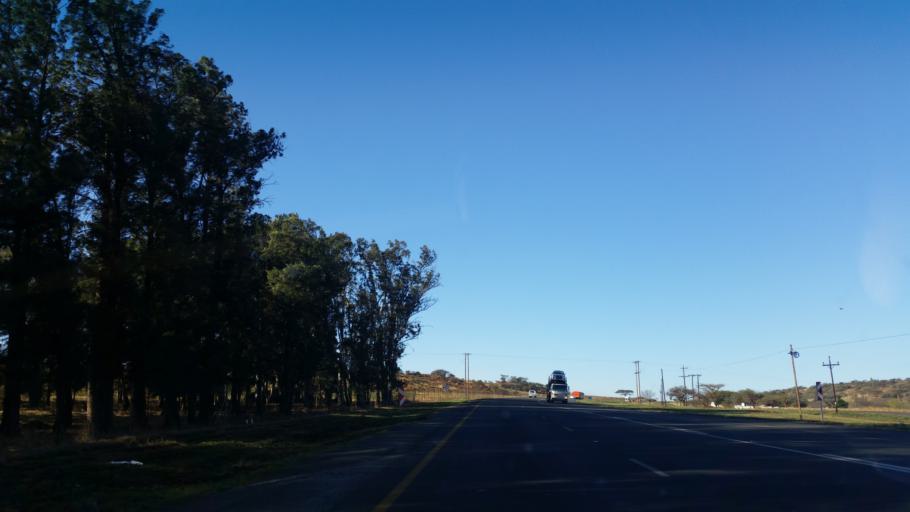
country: ZA
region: KwaZulu-Natal
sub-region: Amajuba District Municipality
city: Newcastle
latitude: -27.7992
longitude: 29.9565
